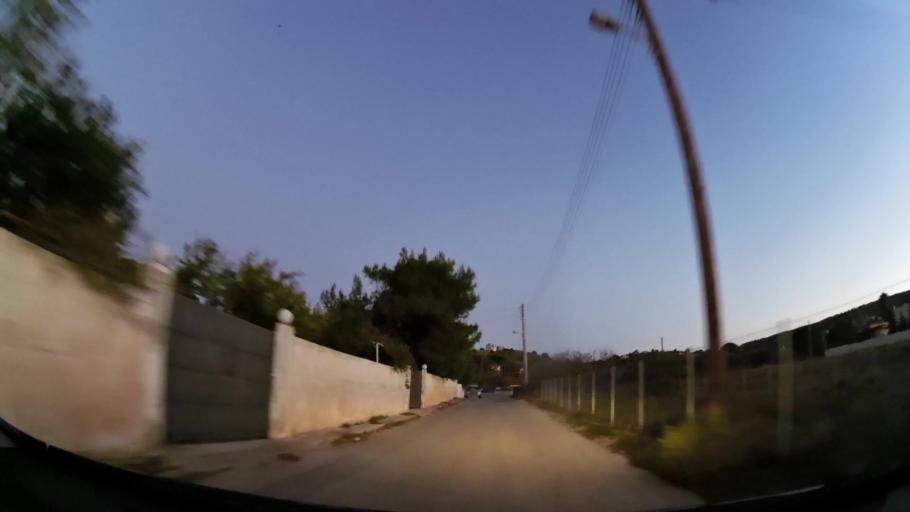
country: GR
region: Attica
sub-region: Nomarchia Anatolikis Attikis
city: Agia Marina
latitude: 37.8234
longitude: 23.8556
